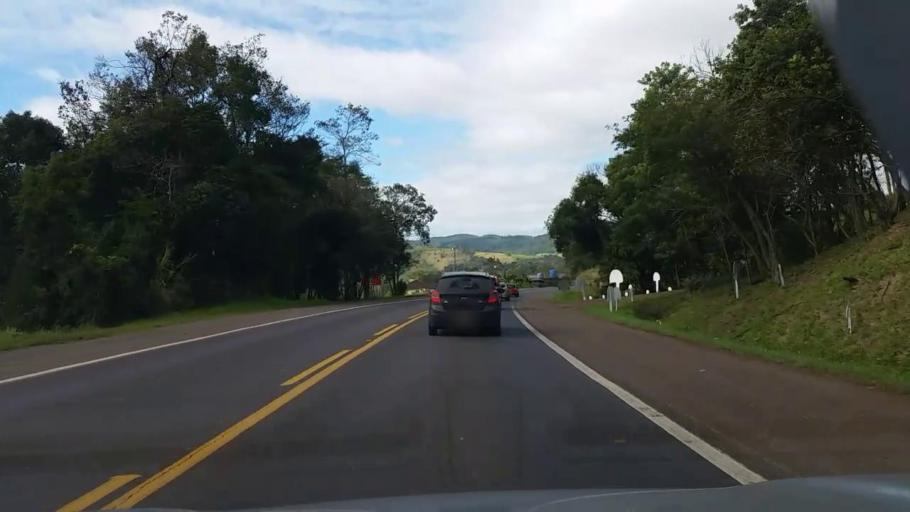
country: BR
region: Rio Grande do Sul
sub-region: Arroio Do Meio
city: Arroio do Meio
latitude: -29.3375
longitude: -52.0816
